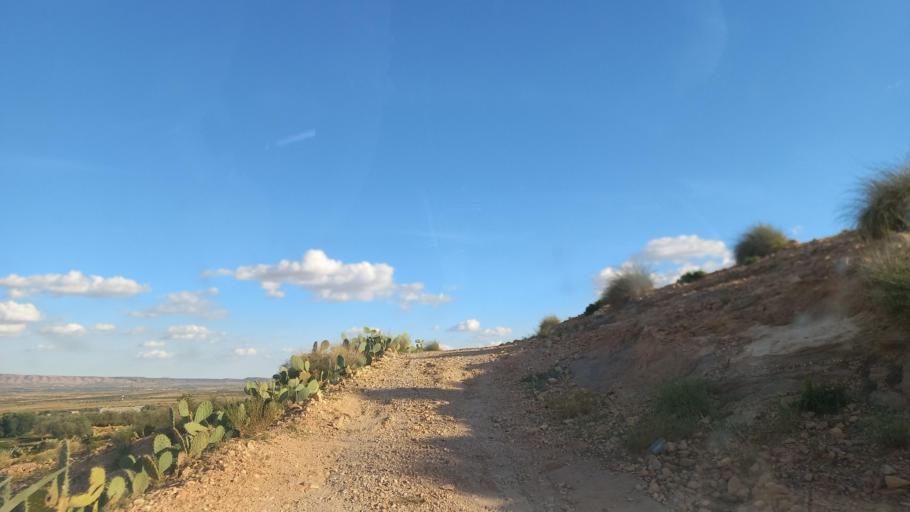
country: TN
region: Al Qasrayn
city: Sbiba
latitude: 35.3809
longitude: 9.0161
